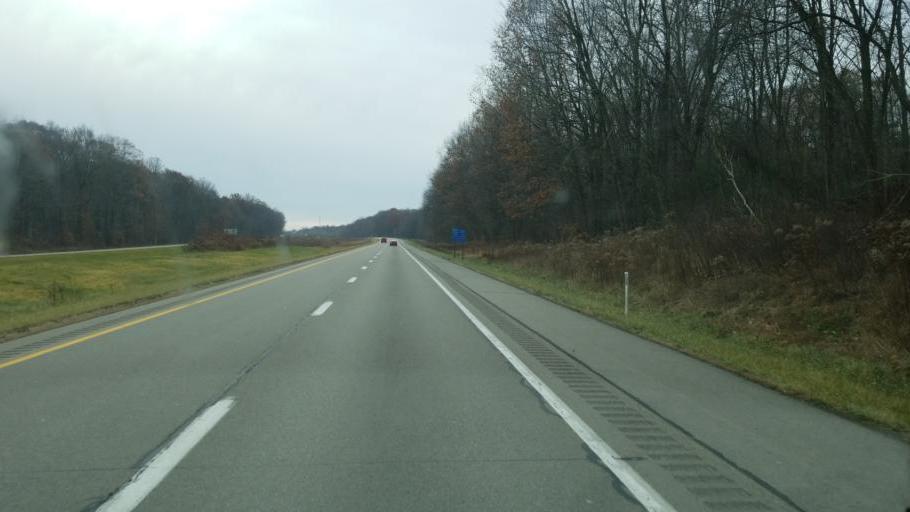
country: US
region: Pennsylvania
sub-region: Crawford County
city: Cochranton
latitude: 41.5182
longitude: -80.1706
